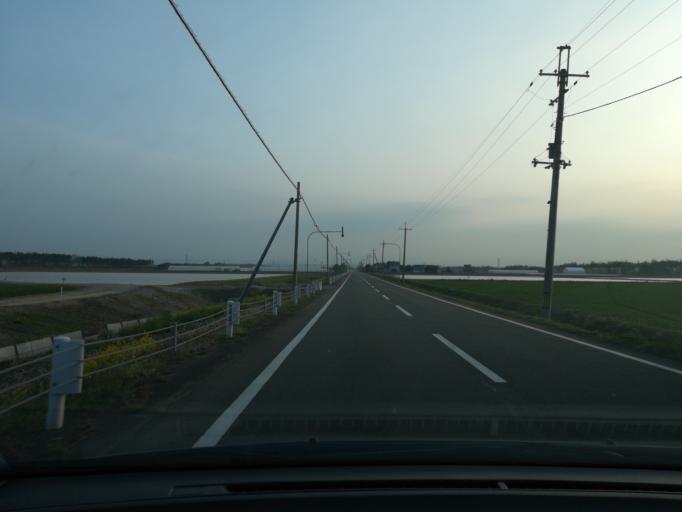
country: JP
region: Hokkaido
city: Ebetsu
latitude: 43.0834
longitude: 141.6194
